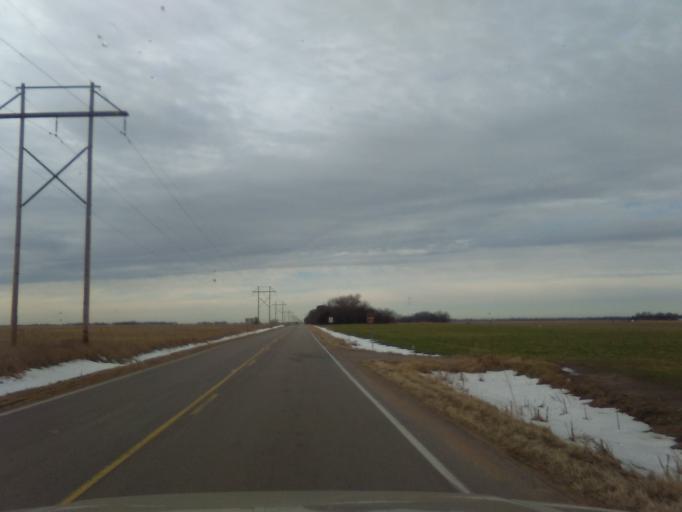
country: US
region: Nebraska
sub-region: Buffalo County
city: Gibbon
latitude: 40.6550
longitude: -98.8007
